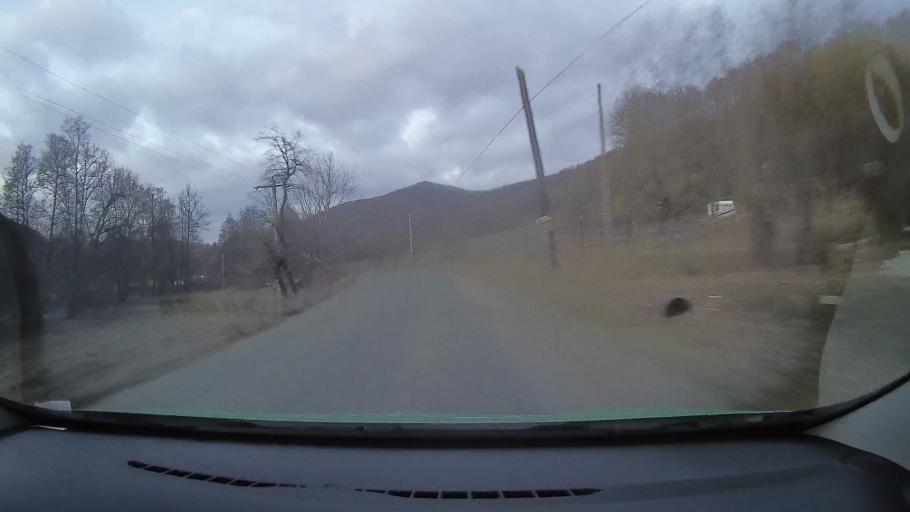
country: RO
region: Dambovita
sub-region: Comuna Valea Lunga
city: Valea Lunga-Cricov
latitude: 45.0832
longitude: 25.5802
